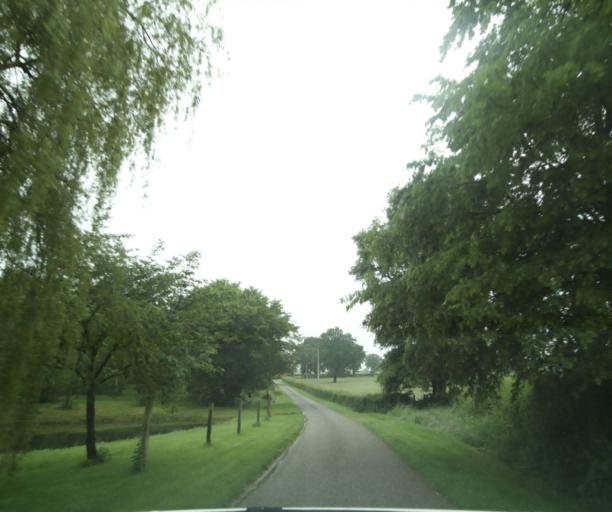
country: FR
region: Bourgogne
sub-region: Departement de Saone-et-Loire
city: Paray-le-Monial
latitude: 46.4079
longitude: 4.1836
